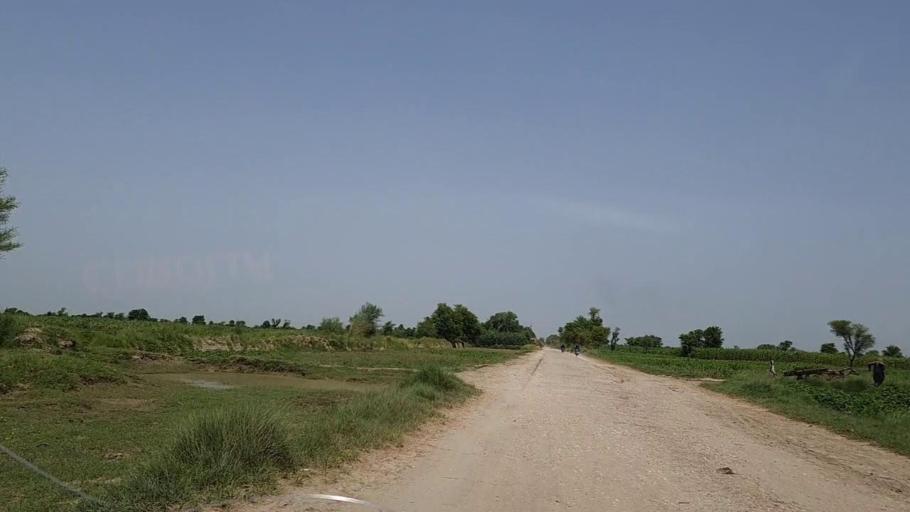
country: PK
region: Sindh
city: Tharu Shah
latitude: 26.9095
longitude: 68.0041
